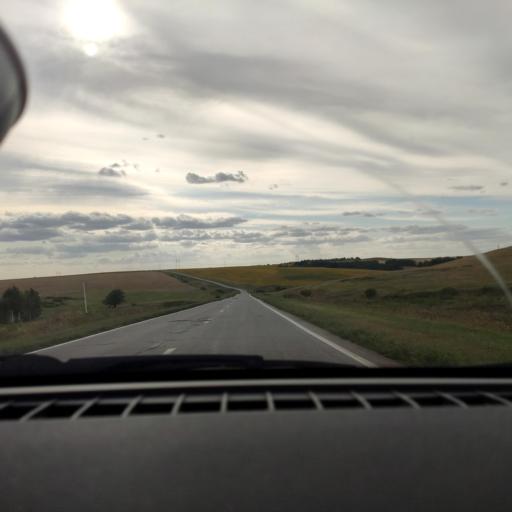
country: RU
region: Samara
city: Kinel'
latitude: 53.4417
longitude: 50.6185
